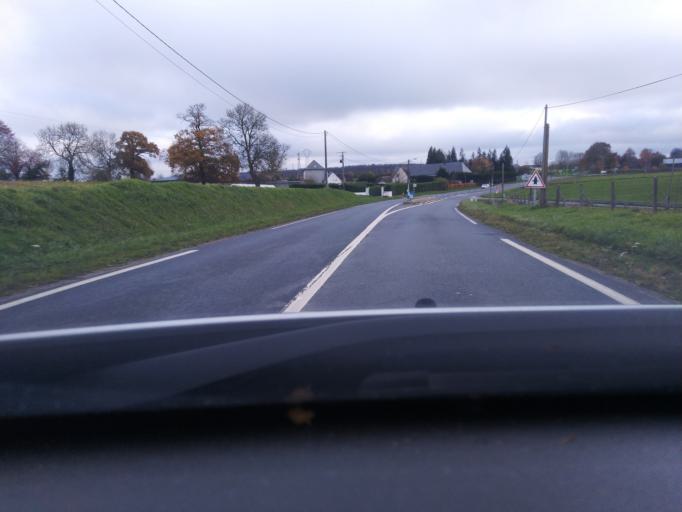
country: FR
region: Haute-Normandie
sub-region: Departement de la Seine-Maritime
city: Roumare
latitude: 49.4994
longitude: 0.9798
